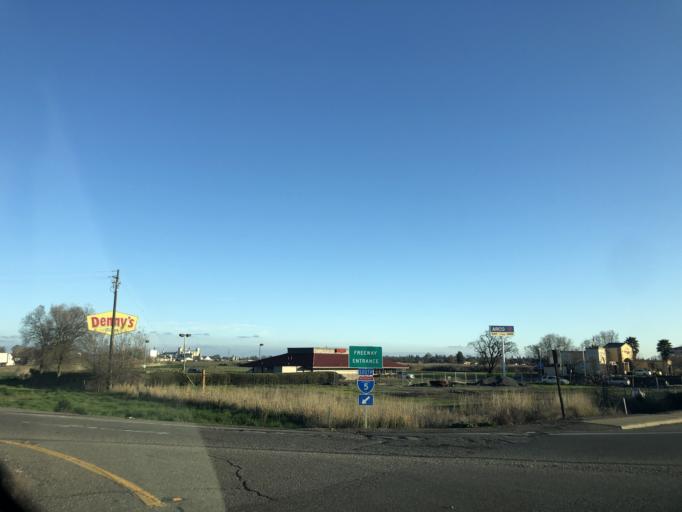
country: US
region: California
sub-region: Yolo County
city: Woodland
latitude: 38.7014
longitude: -121.7839
